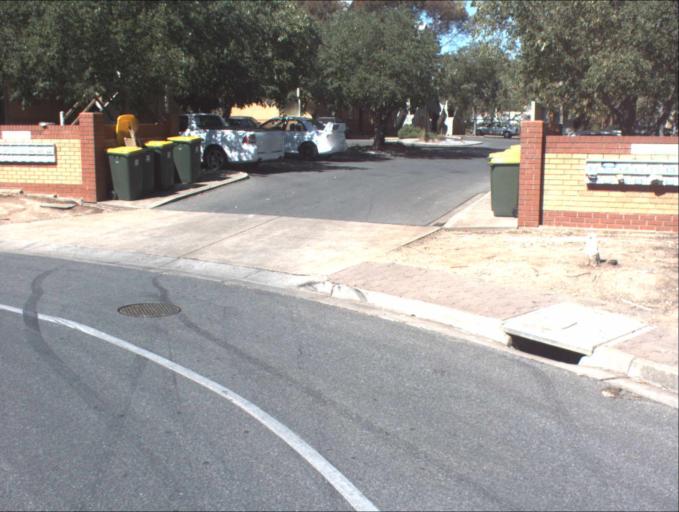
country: AU
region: South Australia
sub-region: Port Adelaide Enfield
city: Blair Athol
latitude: -34.8714
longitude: 138.6082
